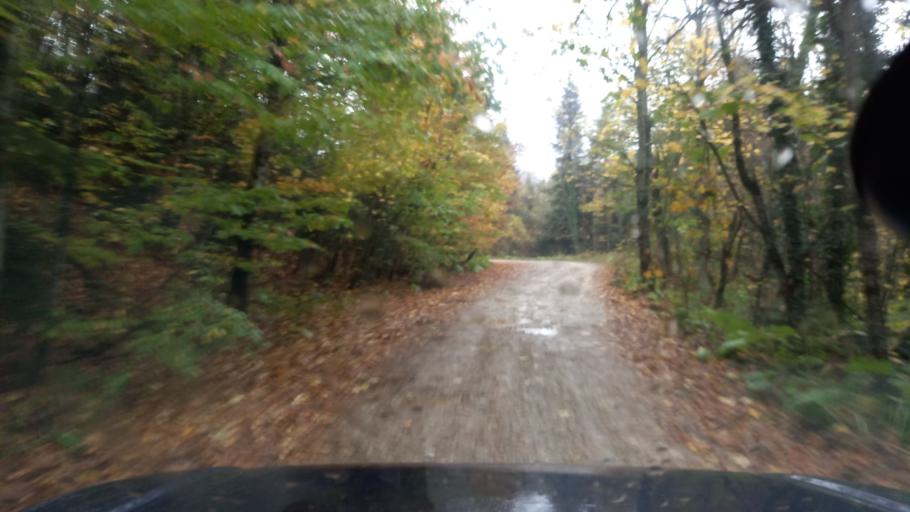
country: RU
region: Krasnodarskiy
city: Neftegorsk
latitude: 44.0374
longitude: 39.8359
